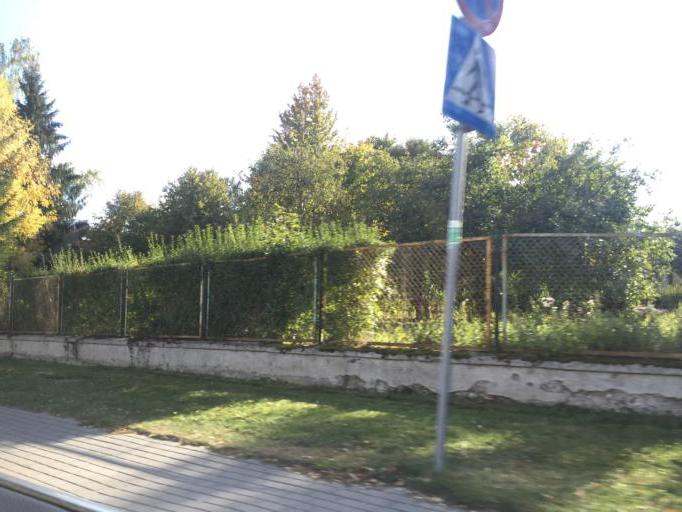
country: PL
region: Warmian-Masurian Voivodeship
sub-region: Powiat bartoszycki
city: Bartoszyce
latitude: 54.2465
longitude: 20.8117
